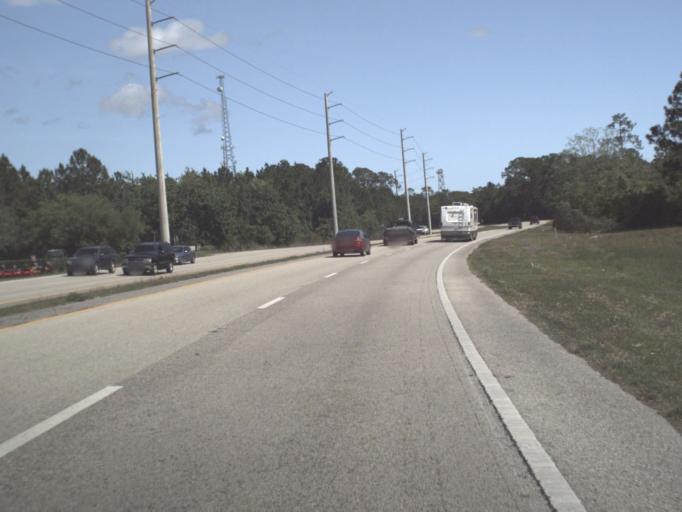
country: US
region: Florida
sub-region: Flagler County
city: Bunnell
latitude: 29.5297
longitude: -81.2631
